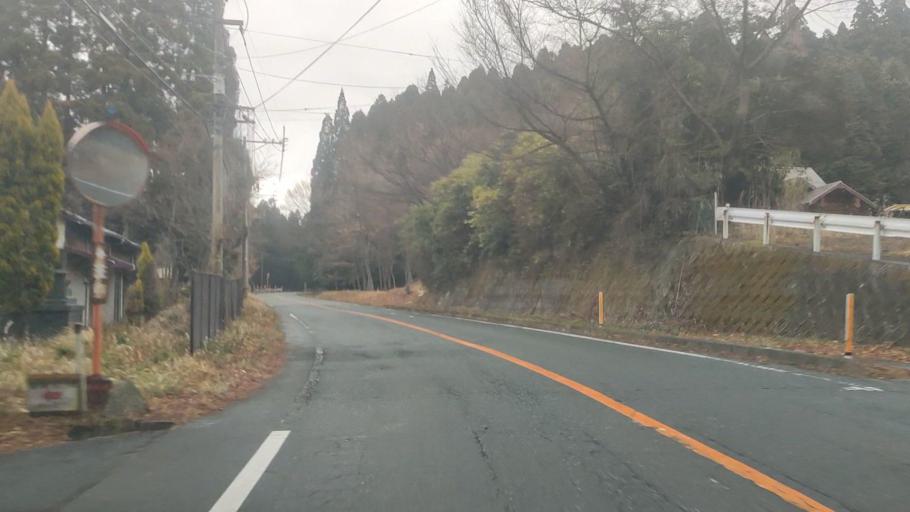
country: JP
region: Kumamoto
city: Aso
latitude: 32.8580
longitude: 131.1616
